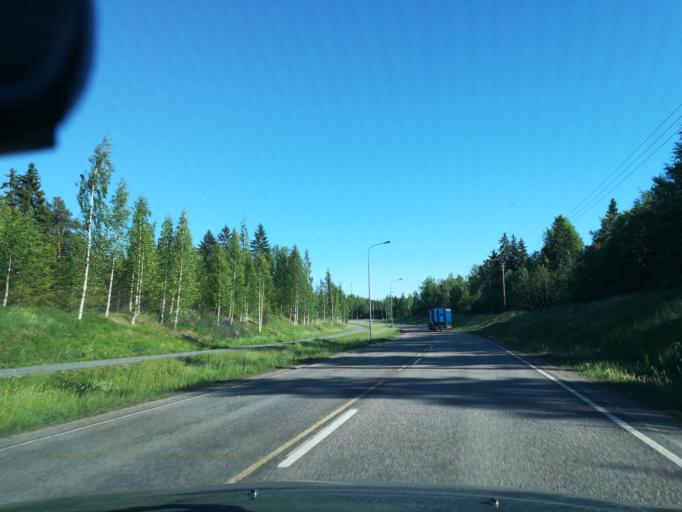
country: FI
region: South Karelia
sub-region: Imatra
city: Imatra
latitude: 61.1604
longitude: 28.7904
